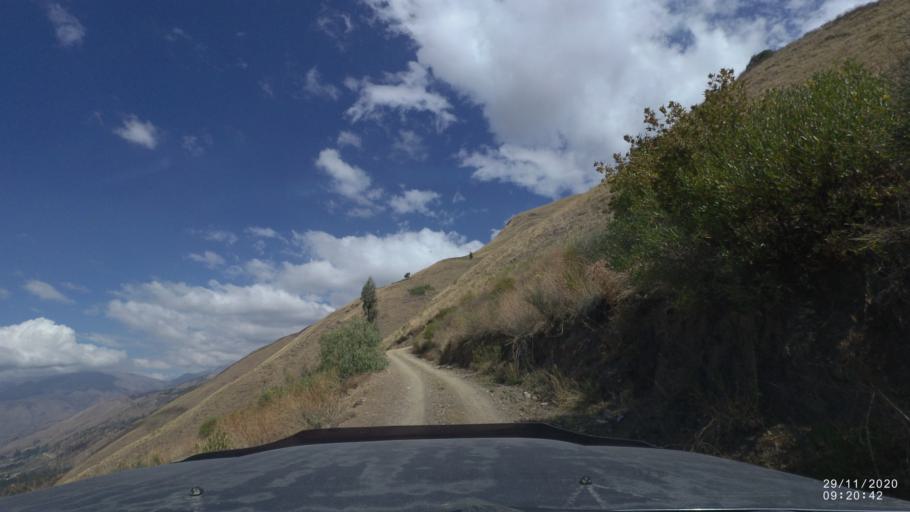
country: BO
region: Cochabamba
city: Cochabamba
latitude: -17.3235
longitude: -66.1870
